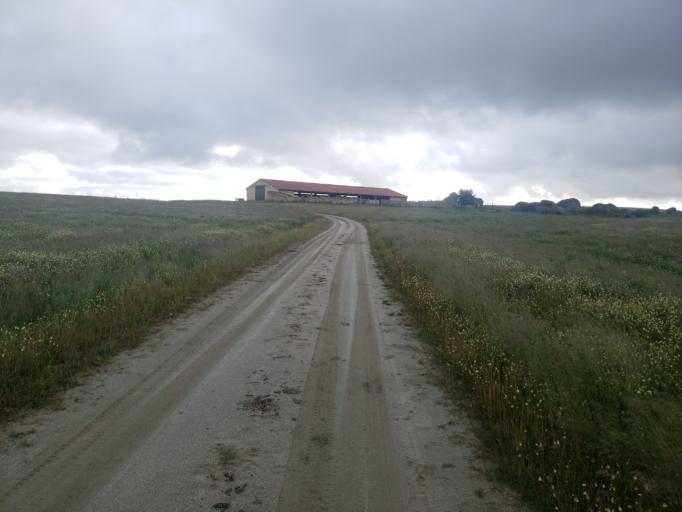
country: ES
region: Extremadura
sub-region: Provincia de Caceres
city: Malpartida de Caceres
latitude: 39.4288
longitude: -6.4924
